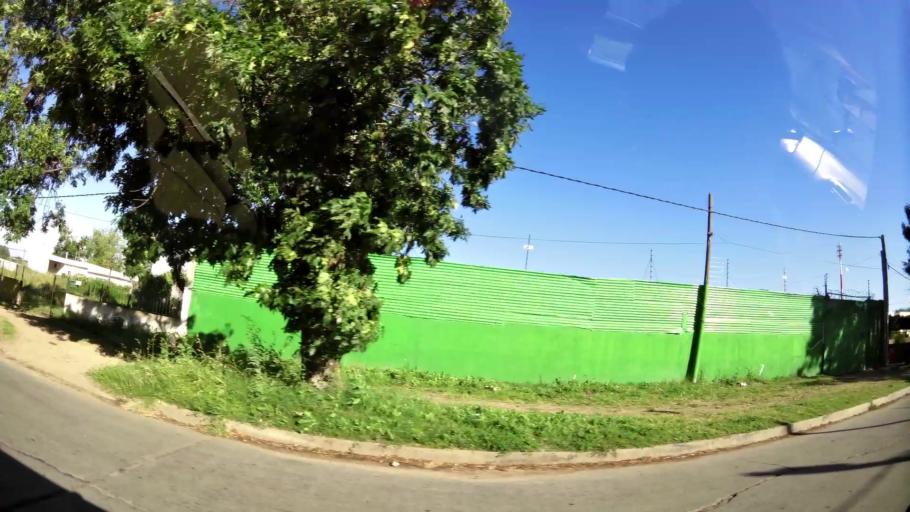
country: UY
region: Canelones
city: La Paz
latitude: -34.8373
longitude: -56.2383
